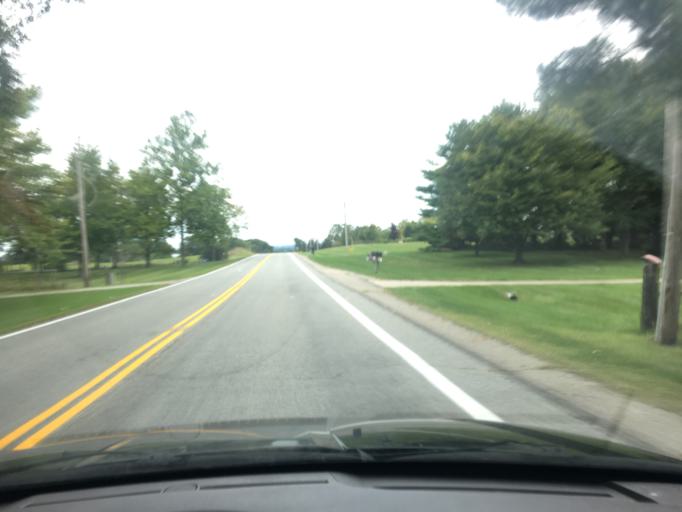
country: US
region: Ohio
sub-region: Champaign County
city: Urbana
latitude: 40.1529
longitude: -83.7114
